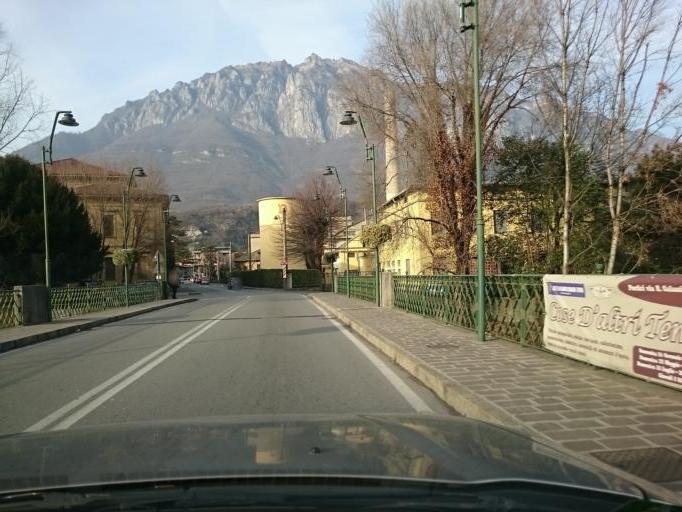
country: IT
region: Lombardy
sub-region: Provincia di Brescia
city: Darfo
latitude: 45.8810
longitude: 10.1825
